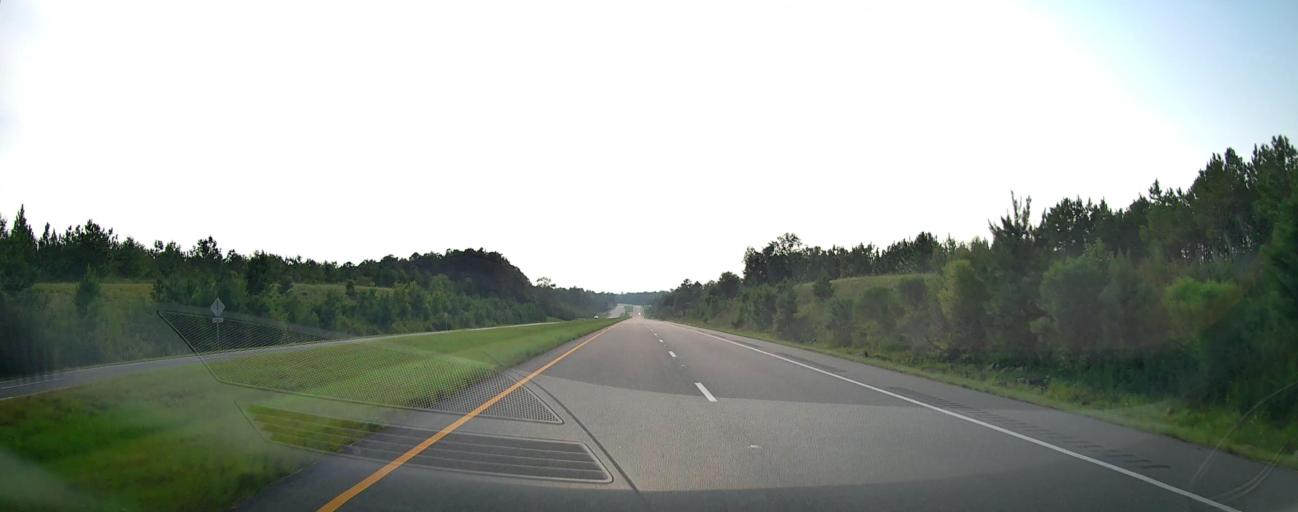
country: US
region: Georgia
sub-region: Talbot County
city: Talbotton
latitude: 32.5789
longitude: -84.5330
